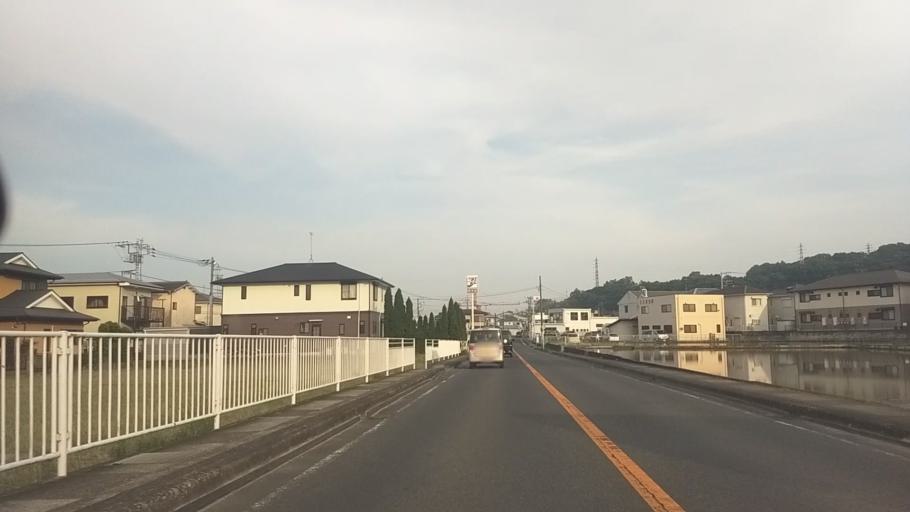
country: JP
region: Kanagawa
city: Odawara
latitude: 35.2867
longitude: 139.1394
